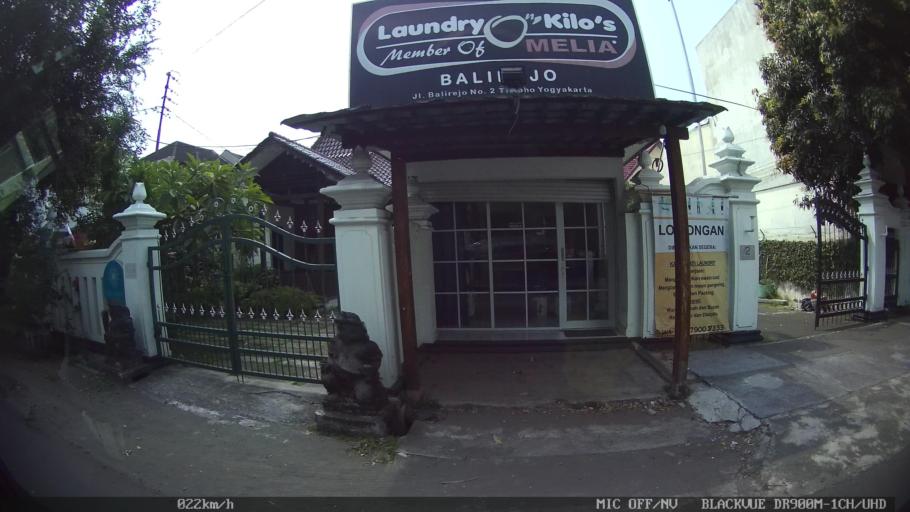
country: ID
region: Daerah Istimewa Yogyakarta
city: Yogyakarta
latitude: -7.7985
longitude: 110.3942
